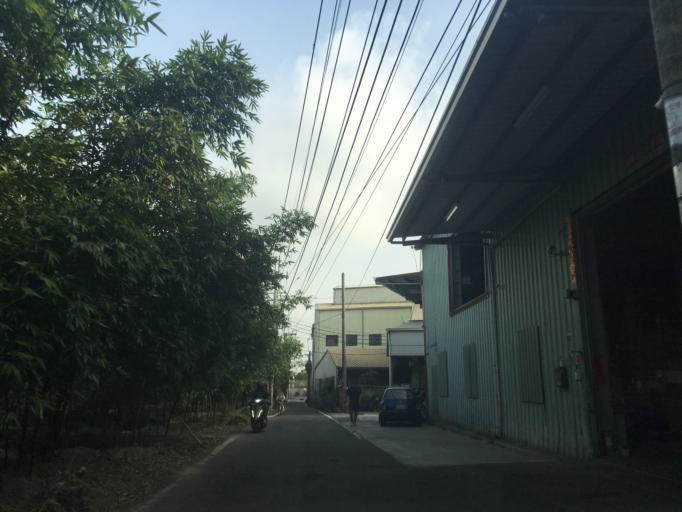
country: TW
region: Taiwan
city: Fengyuan
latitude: 24.2299
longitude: 120.7270
